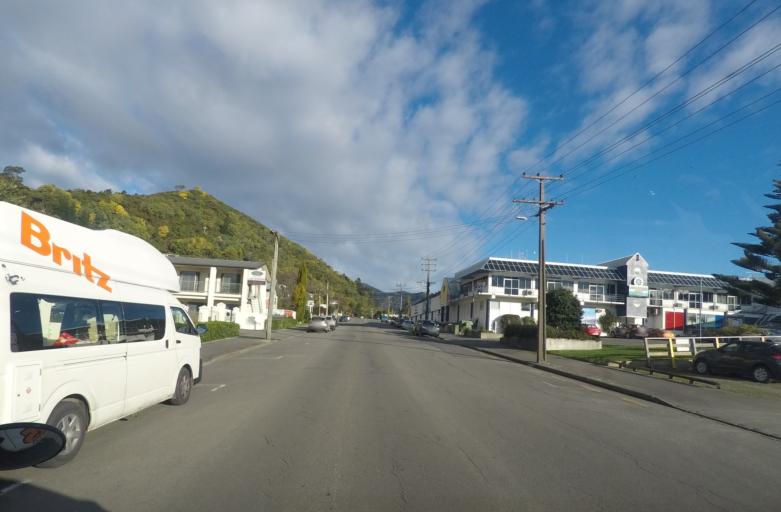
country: NZ
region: Marlborough
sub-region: Marlborough District
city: Picton
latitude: -41.2914
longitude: 174.0079
